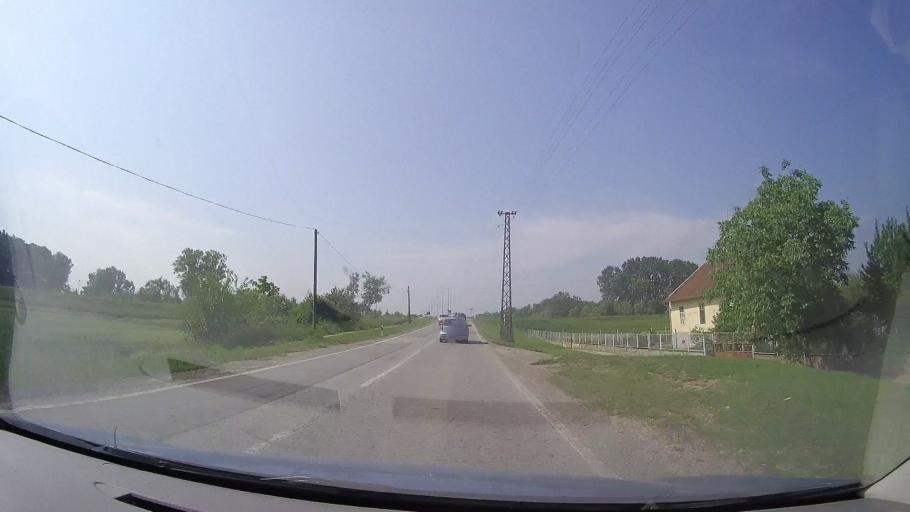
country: RS
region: Autonomna Pokrajina Vojvodina
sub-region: Srednjebanatski Okrug
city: Secanj
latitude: 45.3601
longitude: 20.7712
